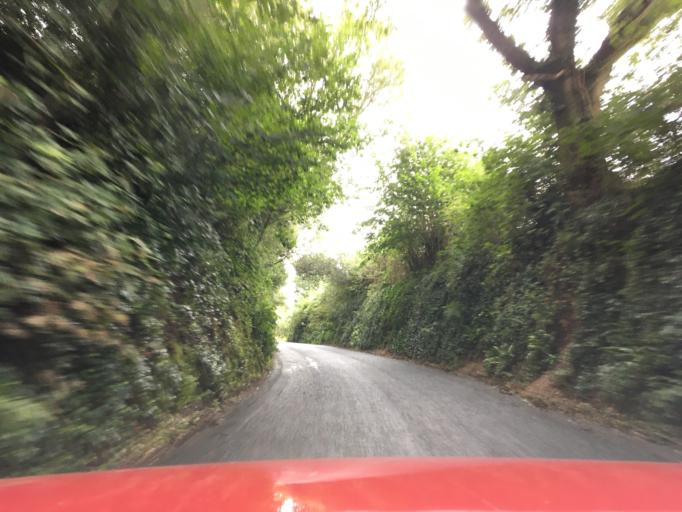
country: GB
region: England
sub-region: Devon
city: Modbury
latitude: 50.3163
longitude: -3.8379
